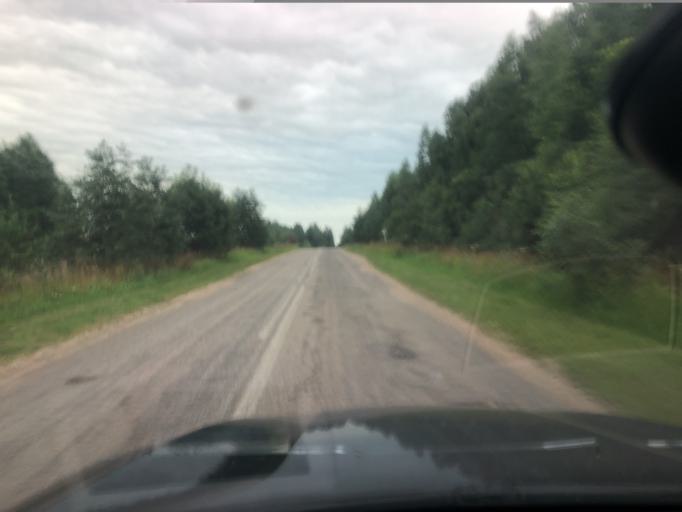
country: RU
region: Jaroslavl
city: Pereslavl'-Zalesskiy
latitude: 57.0275
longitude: 38.9228
